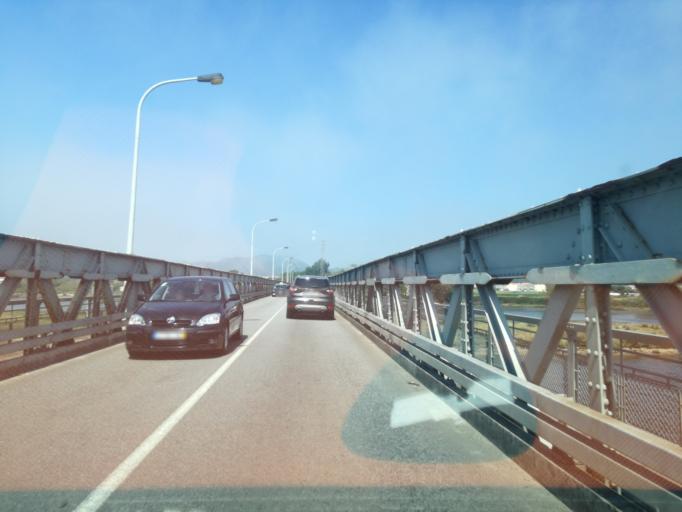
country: PT
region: Braga
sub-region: Esposende
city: Esposende
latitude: 41.5151
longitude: -8.7724
